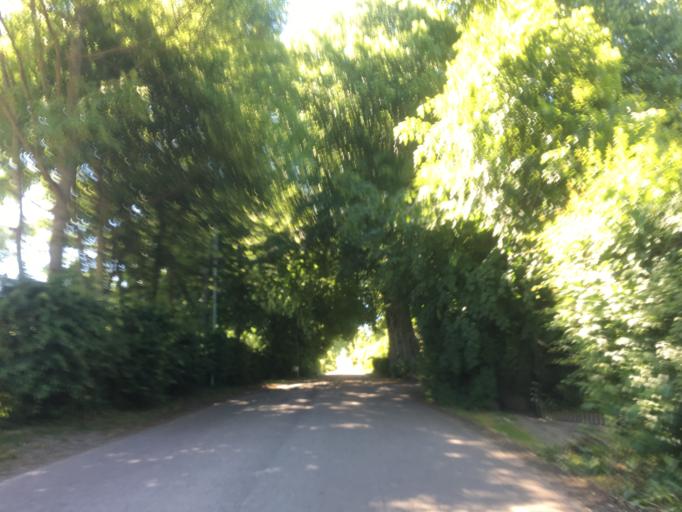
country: SE
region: Skane
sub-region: Helsingborg
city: Rydeback
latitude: 55.9133
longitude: 12.6890
